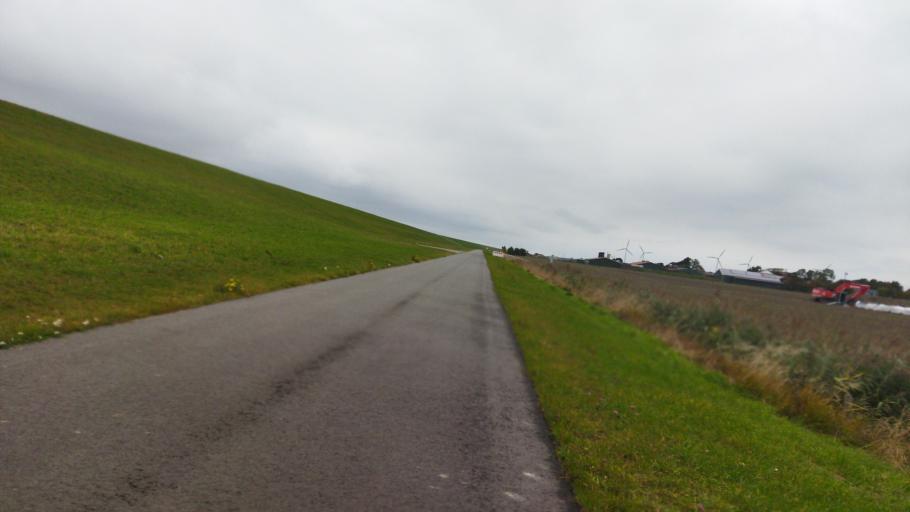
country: NL
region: Groningen
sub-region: Gemeente Delfzijl
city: Delfzijl
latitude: 53.4258
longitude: 7.0151
